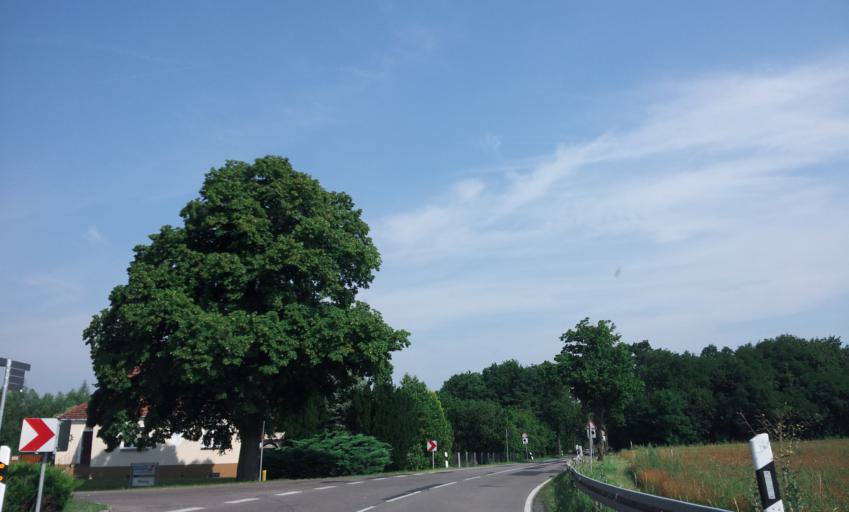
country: DE
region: Brandenburg
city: Linthe
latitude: 52.1300
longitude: 12.7971
